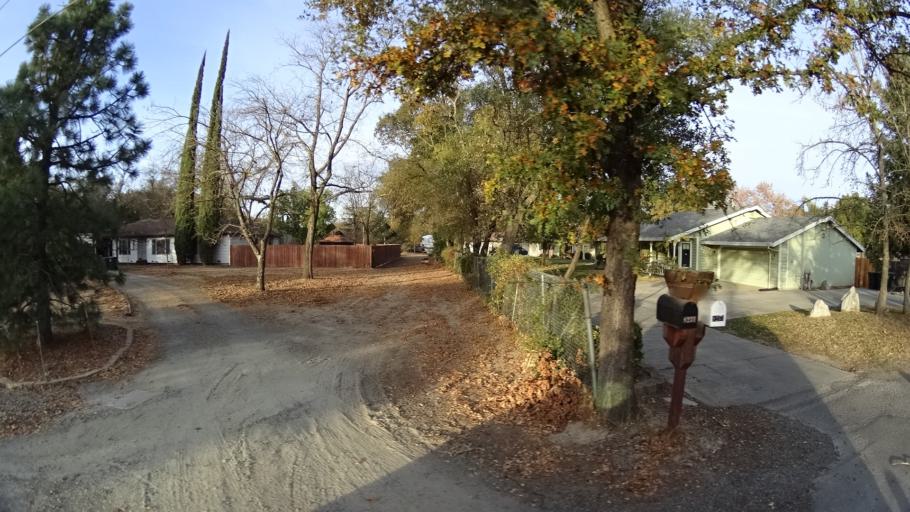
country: US
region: California
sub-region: Sacramento County
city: Citrus Heights
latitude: 38.7158
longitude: -121.2789
